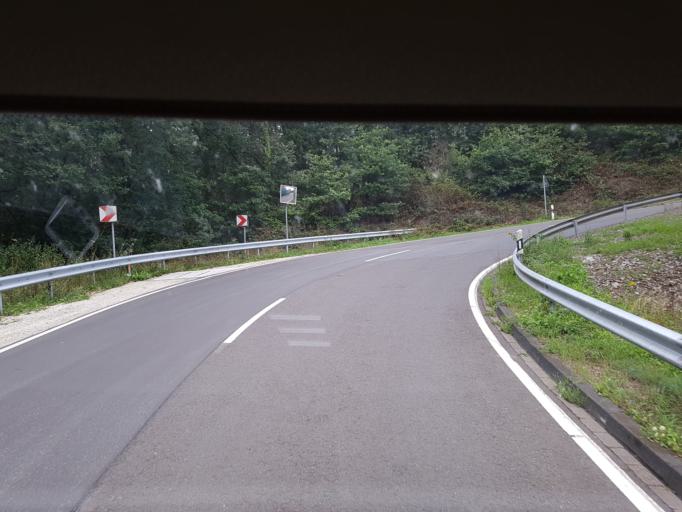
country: DE
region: Rheinland-Pfalz
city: Enkirch
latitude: 49.9876
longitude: 7.1051
